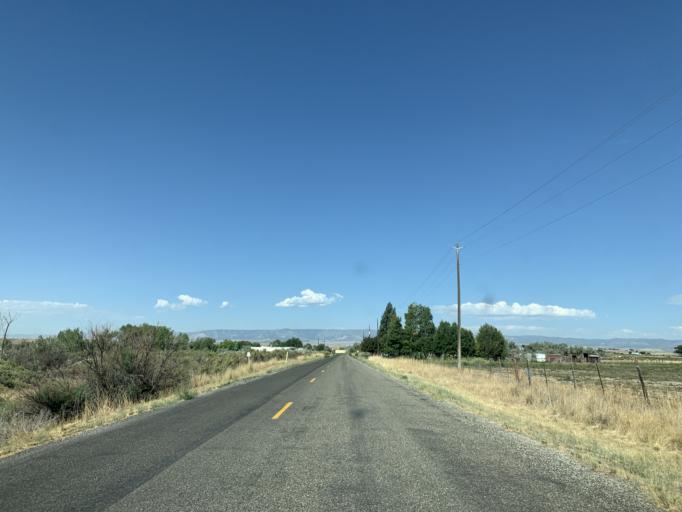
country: US
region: Utah
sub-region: Carbon County
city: Wellington
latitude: 39.5500
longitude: -110.6768
